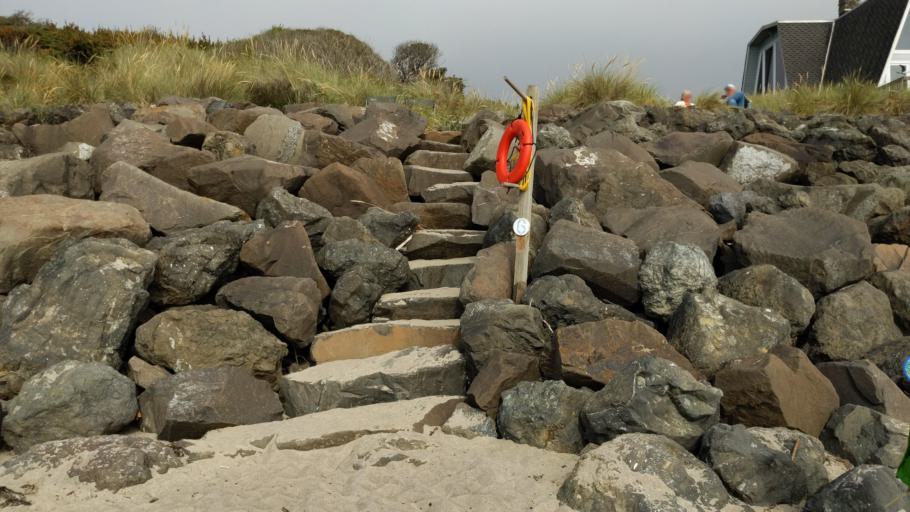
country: US
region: Oregon
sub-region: Tillamook County
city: Pacific City
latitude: 45.1051
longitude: -123.9851
